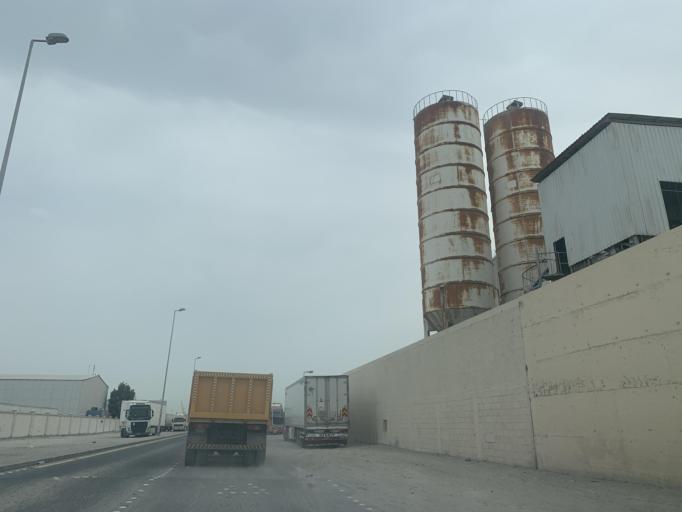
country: BH
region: Muharraq
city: Al Hadd
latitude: 26.2063
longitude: 50.6626
